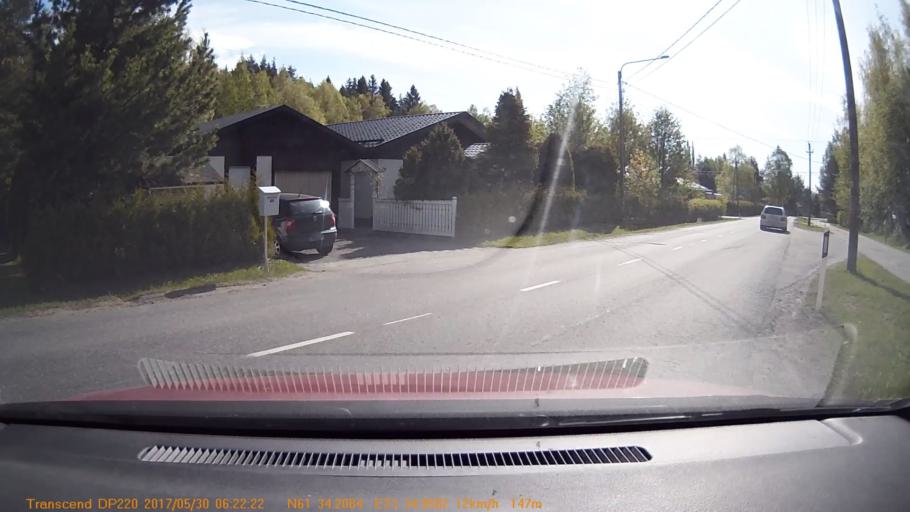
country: FI
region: Pirkanmaa
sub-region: Tampere
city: Yloejaervi
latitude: 61.5701
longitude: 23.5826
